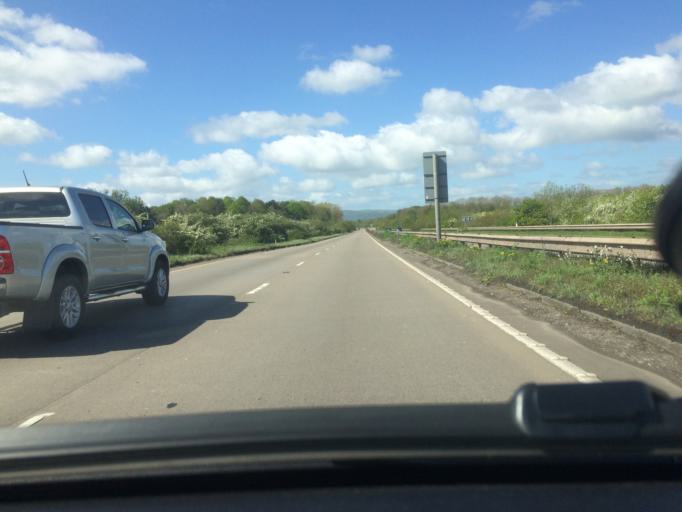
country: GB
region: England
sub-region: Cheshire West and Chester
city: Eccleston
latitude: 53.1486
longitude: -2.9228
